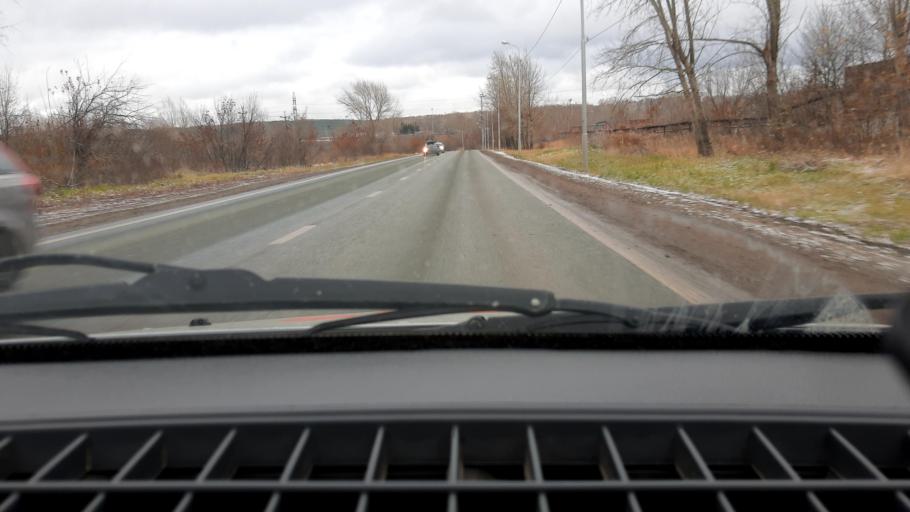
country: RU
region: Bashkortostan
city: Ufa
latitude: 54.8430
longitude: 56.1220
